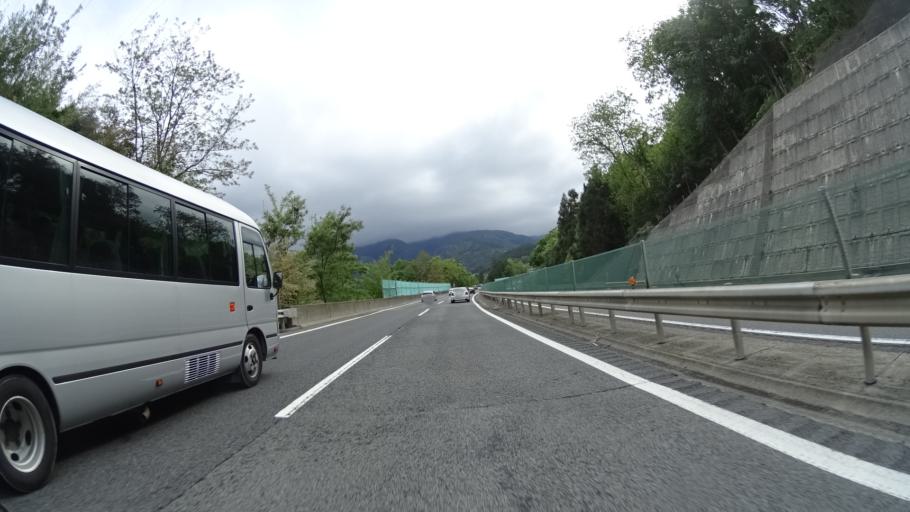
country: JP
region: Nagano
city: Nagano-shi
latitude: 36.5306
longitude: 138.0855
